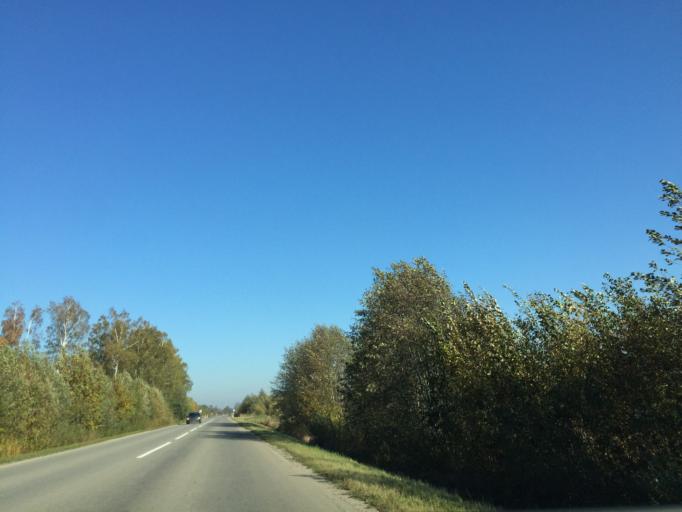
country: LT
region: Klaipedos apskritis
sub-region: Klaipeda
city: Klaipeda
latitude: 55.7778
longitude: 21.2028
